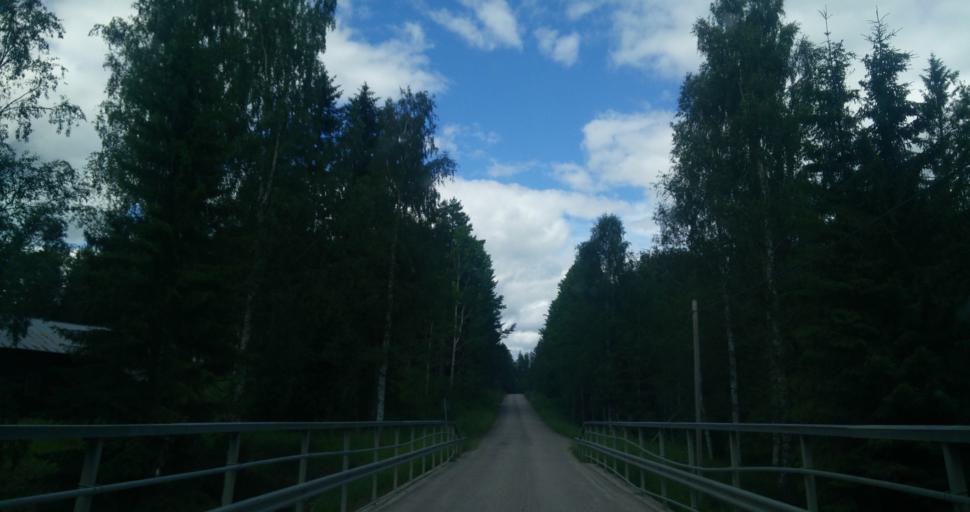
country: SE
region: Gaevleborg
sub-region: Nordanstigs Kommun
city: Bergsjoe
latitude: 62.0552
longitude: 16.8329
